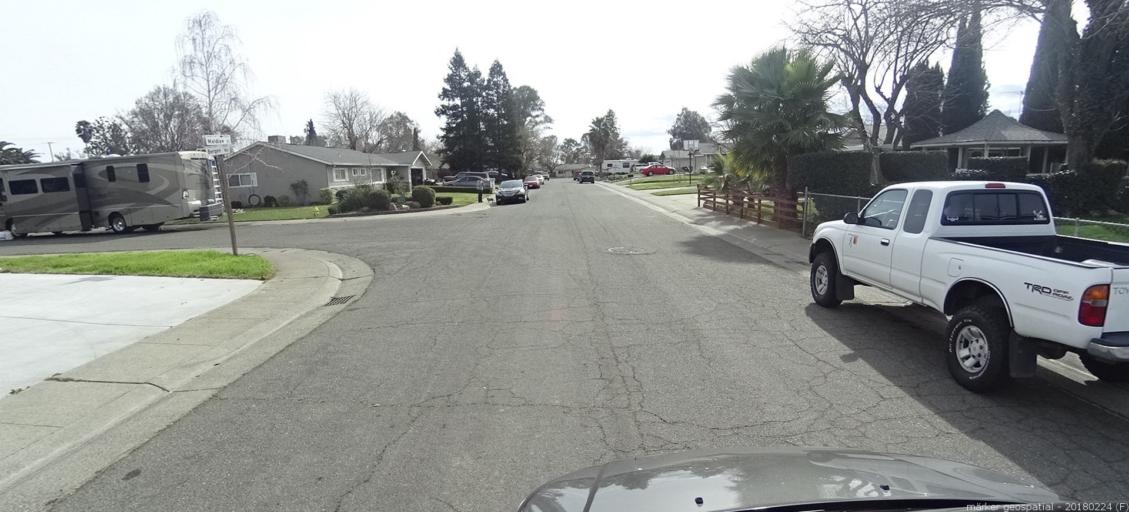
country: US
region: California
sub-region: Sacramento County
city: Elverta
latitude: 38.7047
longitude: -121.4588
